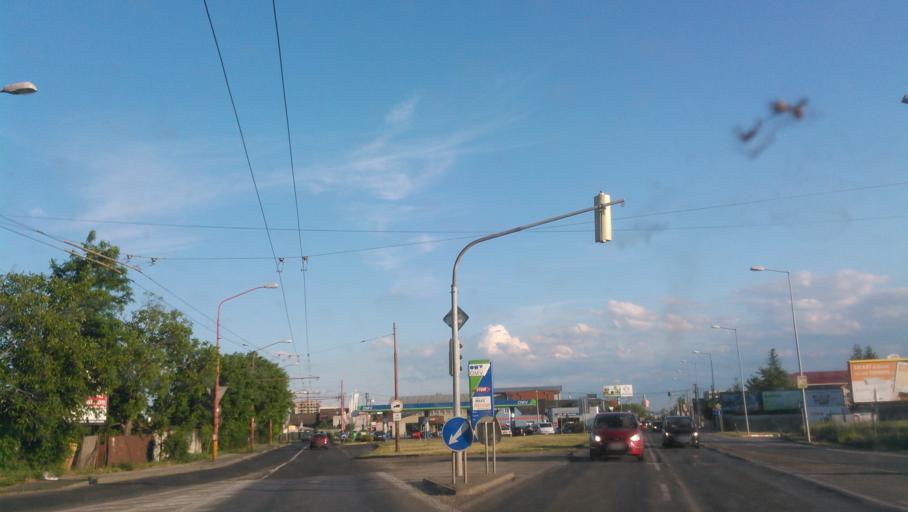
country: SK
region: Bratislavsky
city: Dunajska Luzna
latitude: 48.1387
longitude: 17.1936
